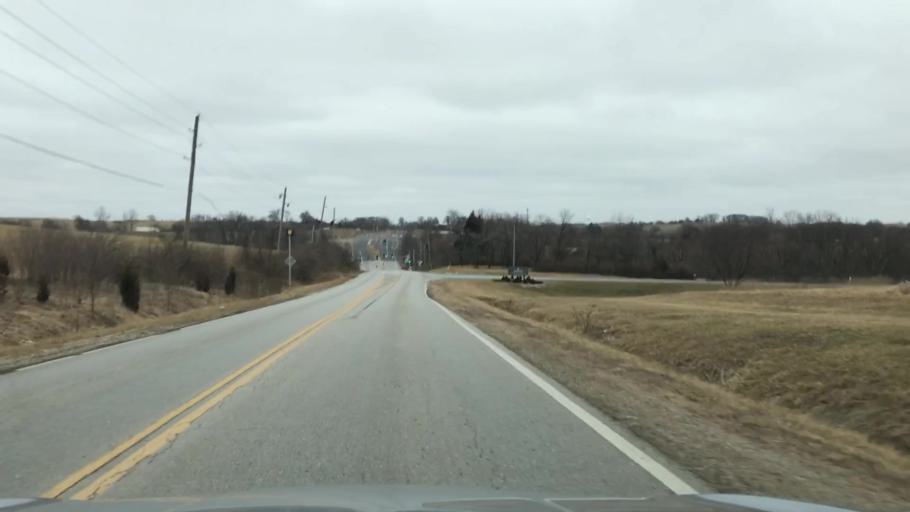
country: US
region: Missouri
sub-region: Clay County
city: Liberty
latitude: 39.2759
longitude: -94.4166
